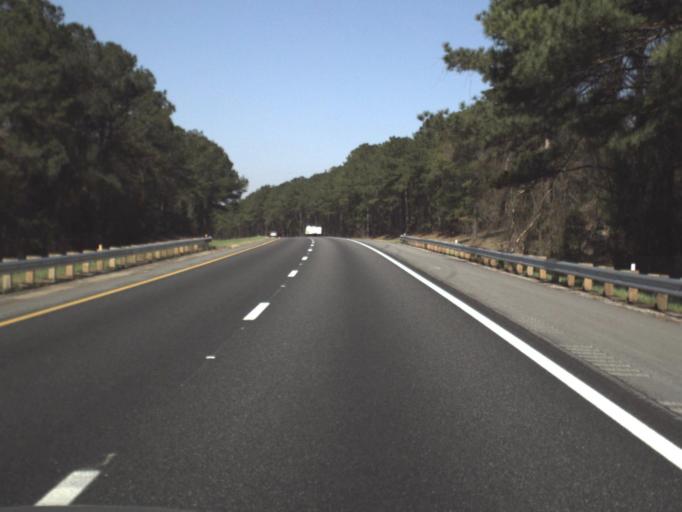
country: US
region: Florida
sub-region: Gadsden County
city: Chattahoochee
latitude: 30.6205
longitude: -84.7739
